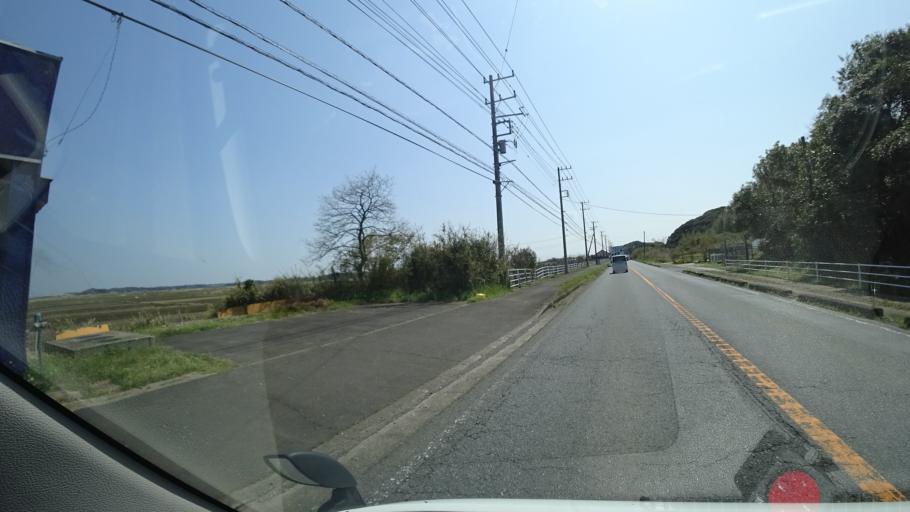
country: JP
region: Chiba
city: Narita
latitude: 35.8415
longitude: 140.3007
